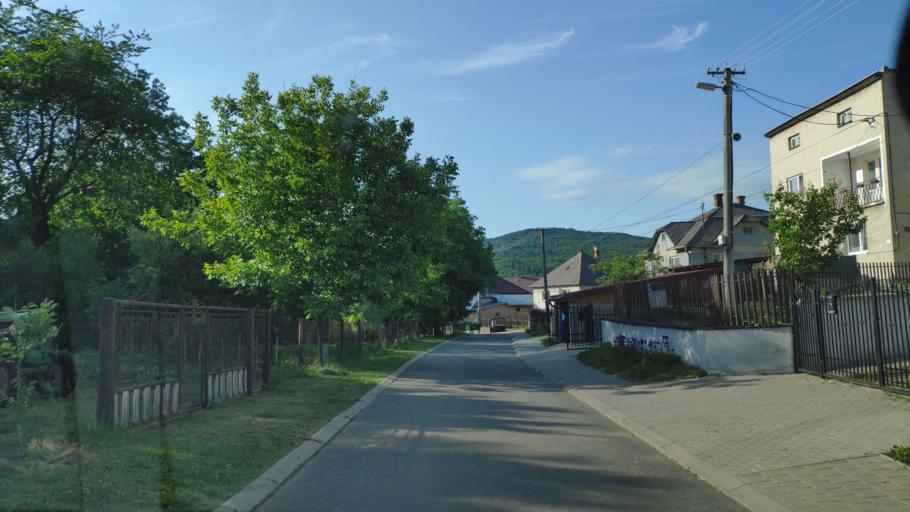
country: SK
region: Presovsky
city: Vranov nad Topl'ou
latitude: 48.8272
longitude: 21.5772
